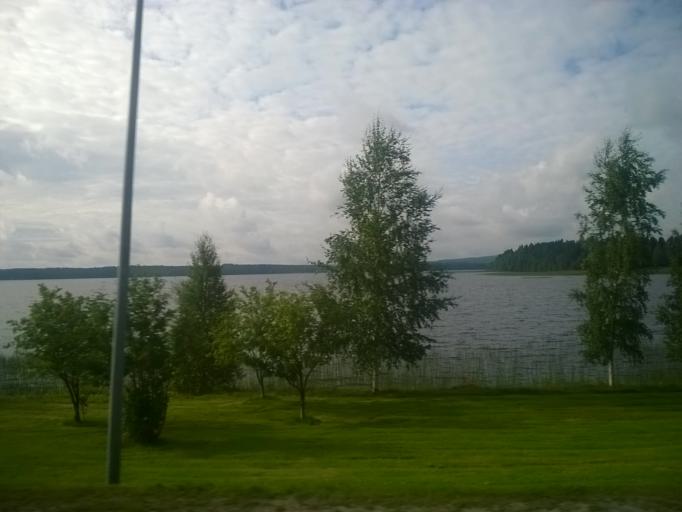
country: FI
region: Kainuu
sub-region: Kajaani
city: Sotkamo
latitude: 64.1340
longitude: 28.3490
